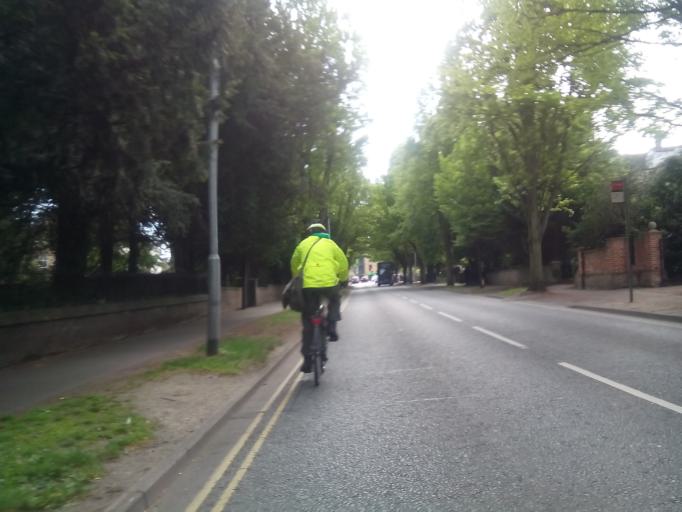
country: GB
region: England
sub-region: Cambridgeshire
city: Cambridge
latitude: 52.1921
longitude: 0.1302
